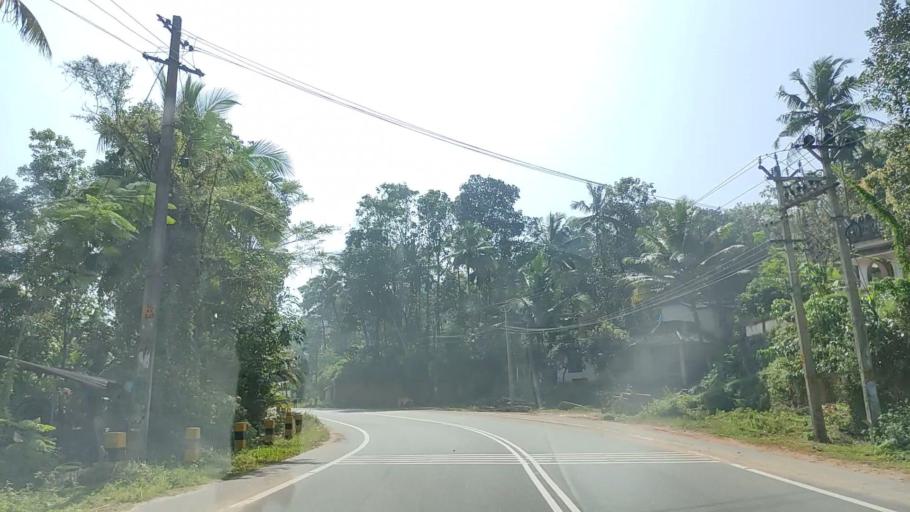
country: IN
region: Kerala
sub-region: Kollam
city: Punalur
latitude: 8.9328
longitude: 76.9632
